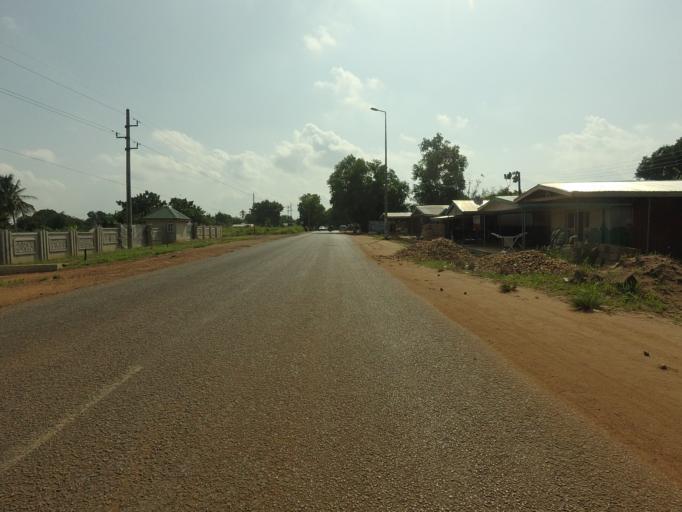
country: GH
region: Volta
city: Ho
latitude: 6.6016
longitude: 0.4958
